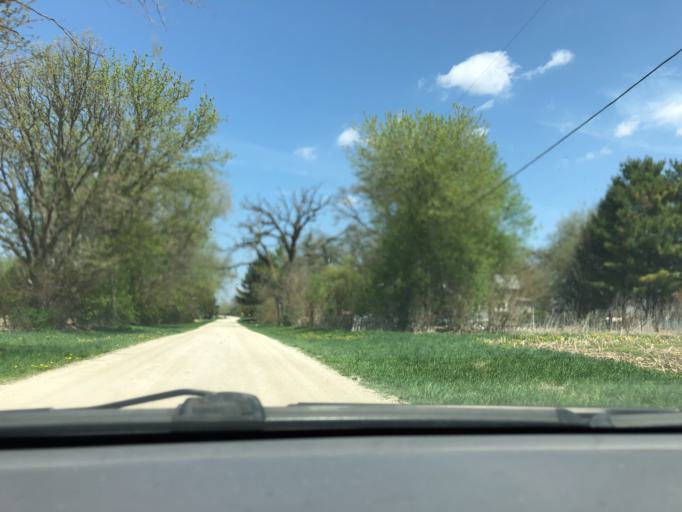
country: US
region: Illinois
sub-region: Kane County
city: Pingree Grove
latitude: 42.0712
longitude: -88.4655
